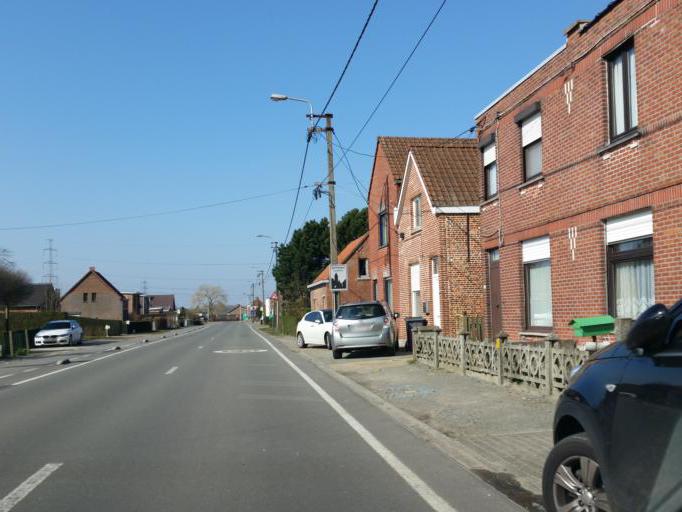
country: BE
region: Flanders
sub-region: Provincie Oost-Vlaanderen
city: Wachtebeke
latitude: 51.1340
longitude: 3.8762
